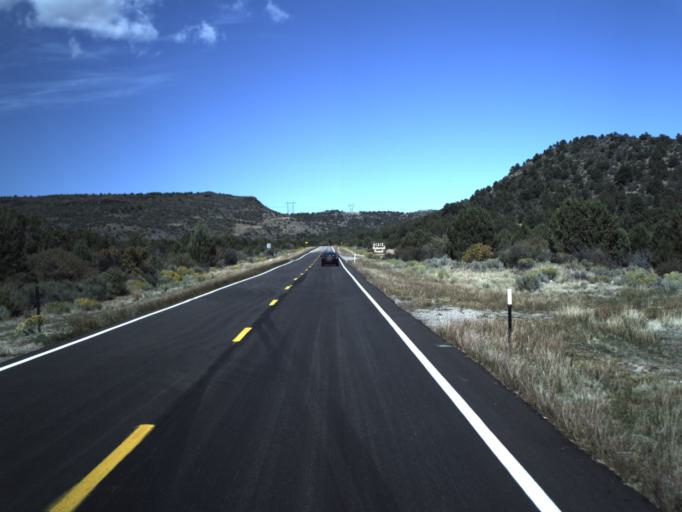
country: US
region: Utah
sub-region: Washington County
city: Enterprise
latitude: 37.4324
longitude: -113.6291
